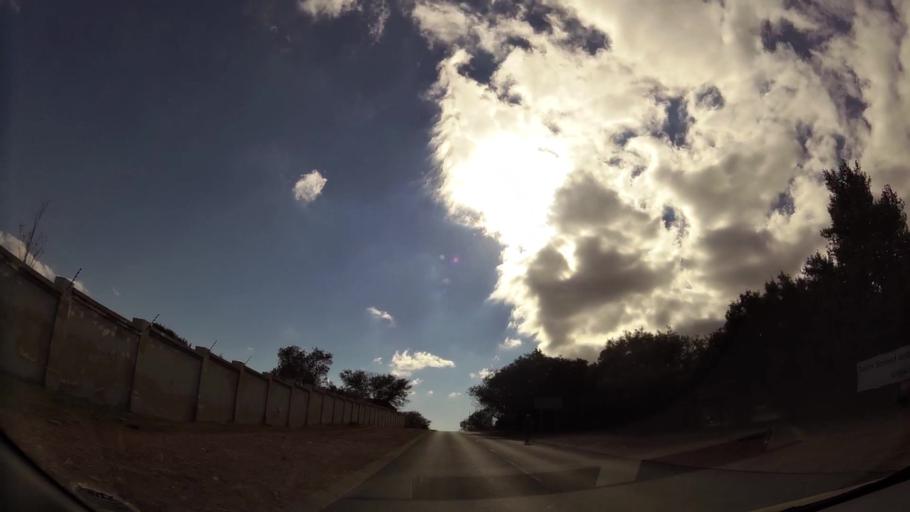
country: ZA
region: Gauteng
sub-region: West Rand District Municipality
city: Muldersdriseloop
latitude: -26.0838
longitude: 27.8545
